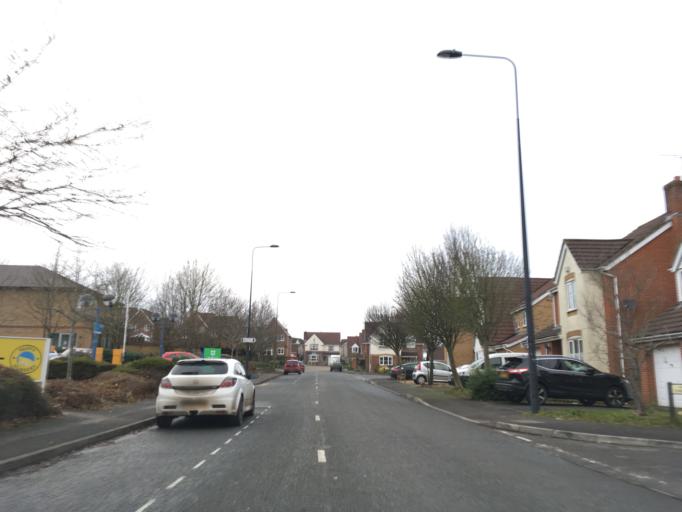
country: GB
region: England
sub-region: South Gloucestershire
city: Stoke Gifford
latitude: 51.5178
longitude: -2.5336
